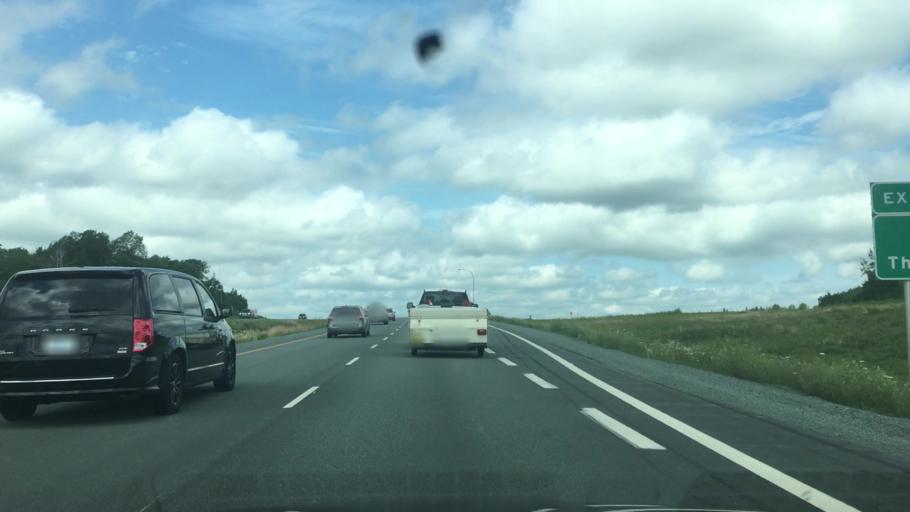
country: CA
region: Nova Scotia
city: Oxford
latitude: 45.6904
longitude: -63.7700
